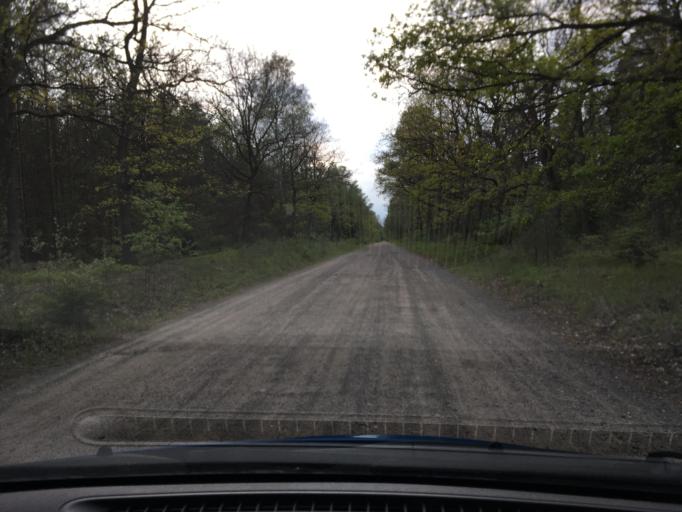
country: DE
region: Lower Saxony
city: Fassberg
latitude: 52.9604
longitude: 10.2069
